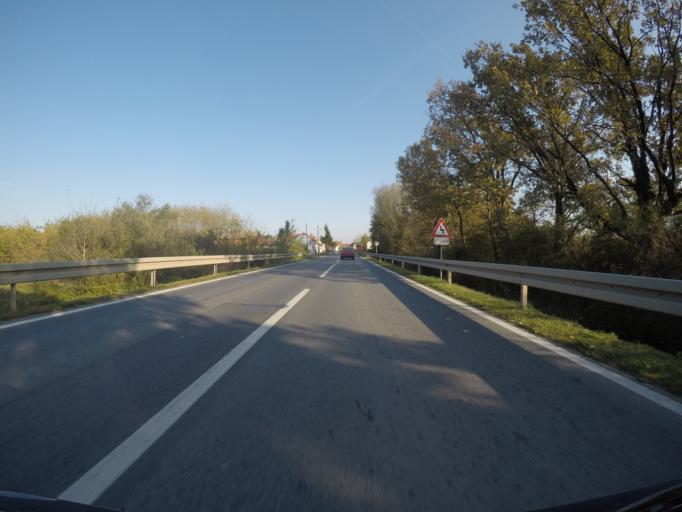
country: HR
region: Virovitick-Podravska
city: Pitomaca
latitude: 45.9648
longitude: 17.2119
